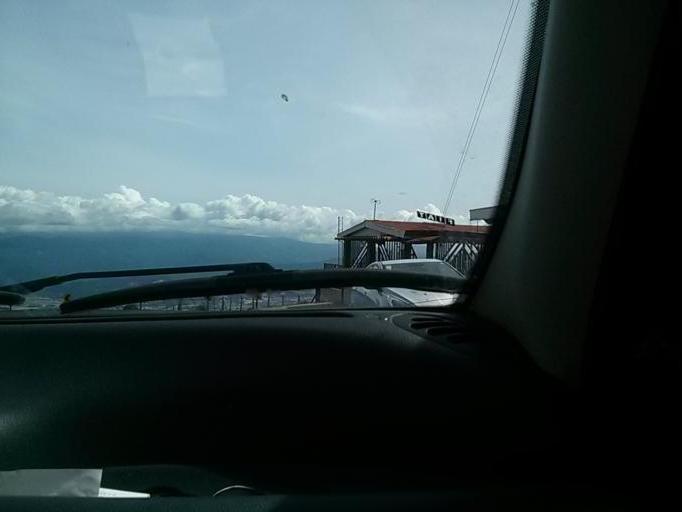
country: CR
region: Cartago
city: Cot
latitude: 9.9154
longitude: -83.8830
